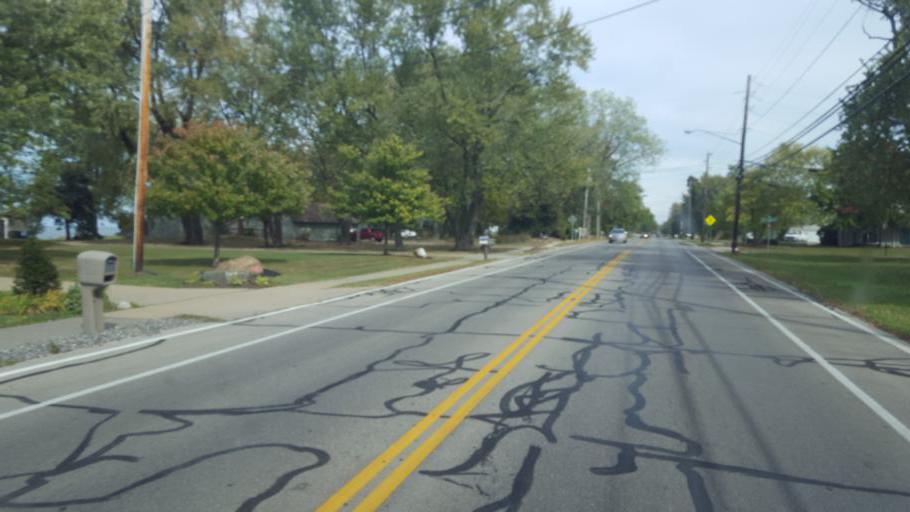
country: US
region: Ohio
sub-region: Lorain County
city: Sheffield Lake
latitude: 41.4953
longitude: -82.0878
